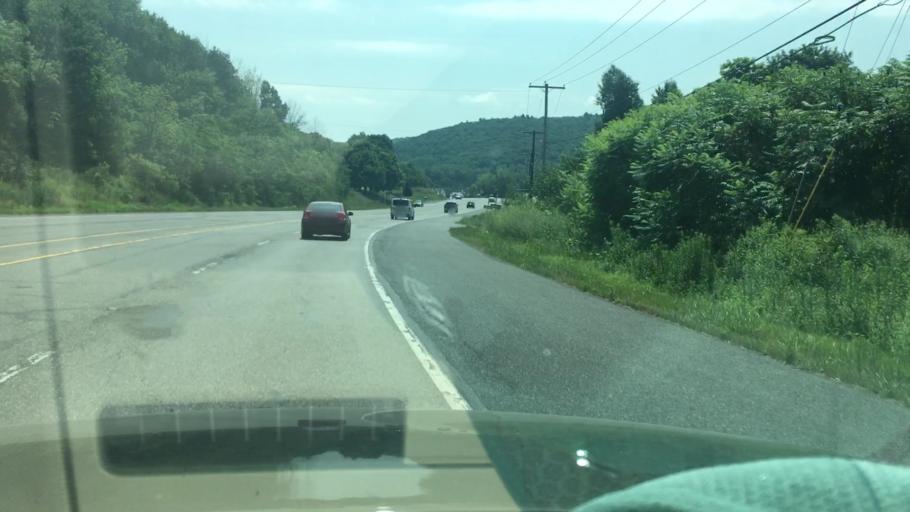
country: US
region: Pennsylvania
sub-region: Schuylkill County
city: Tamaqua
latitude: 40.7626
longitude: -75.9510
